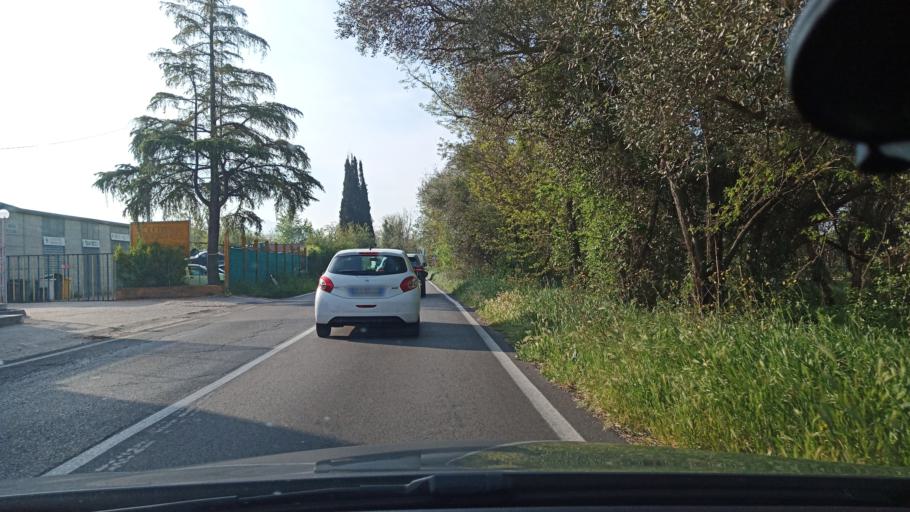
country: IT
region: Latium
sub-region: Citta metropolitana di Roma Capitale
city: Fiano Romano
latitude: 42.1696
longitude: 12.6371
